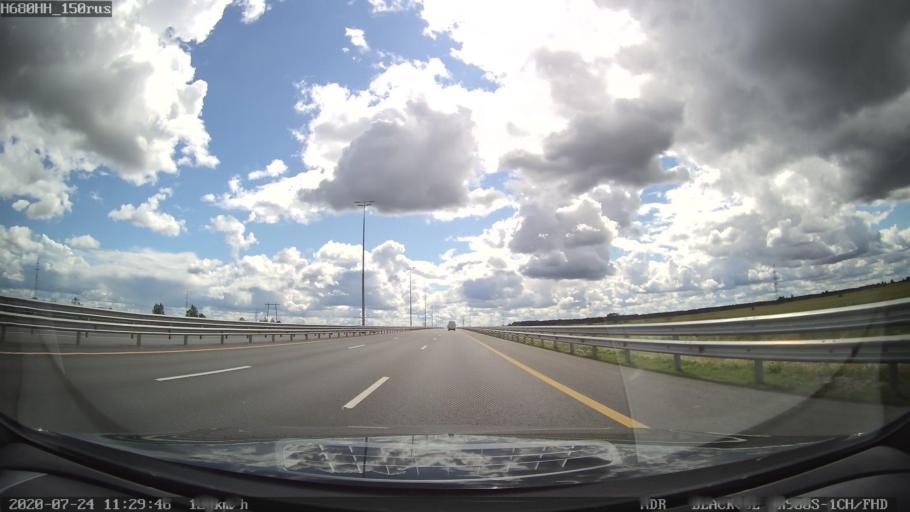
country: RU
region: Leningrad
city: Fedorovskoye
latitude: 59.6789
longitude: 30.5948
